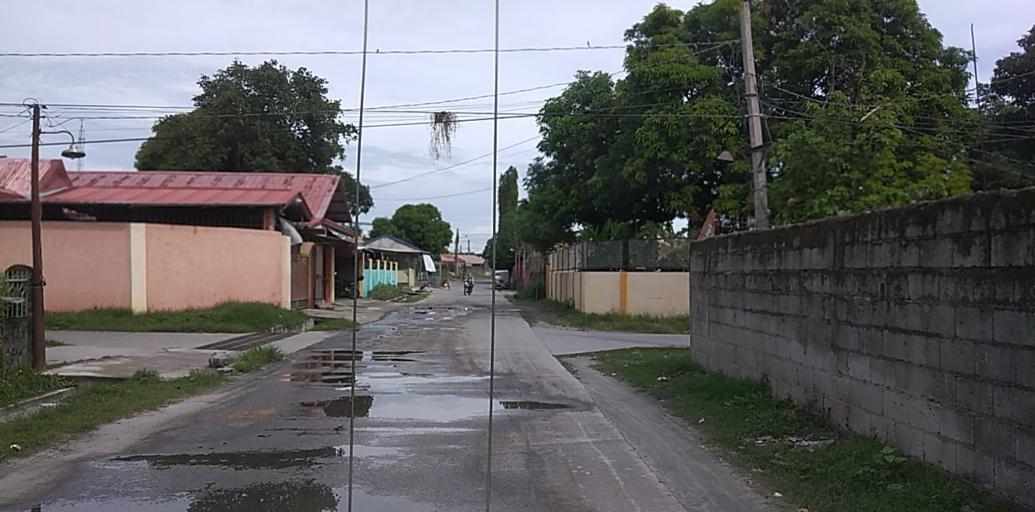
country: PH
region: Central Luzon
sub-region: Province of Pampanga
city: Manibaug Pasig
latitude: 15.1112
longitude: 120.5605
